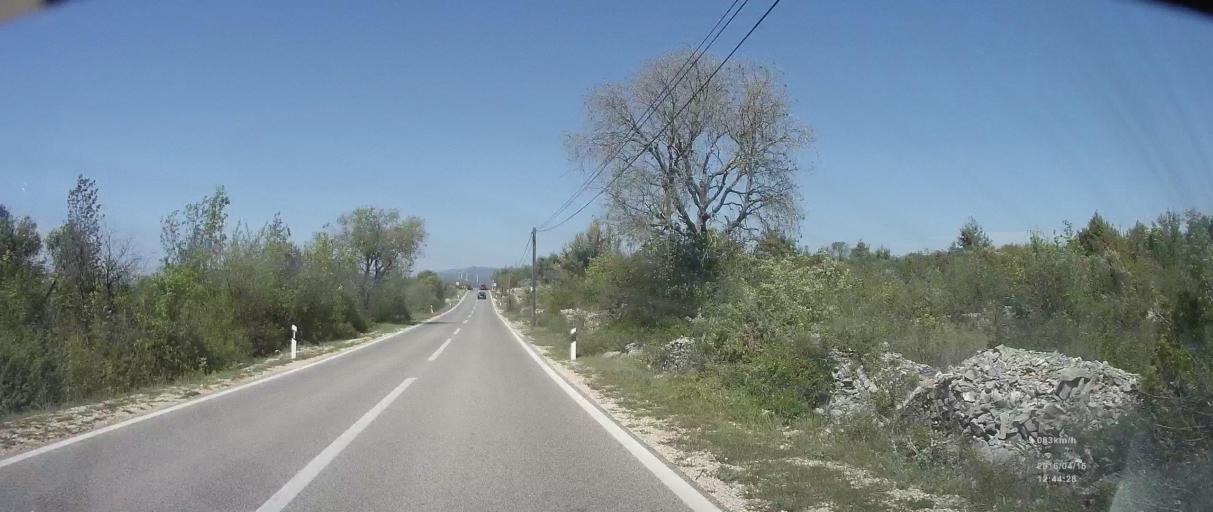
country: HR
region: Sibensko-Kniniska
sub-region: Grad Sibenik
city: Brodarica
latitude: 43.6415
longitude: 16.0646
